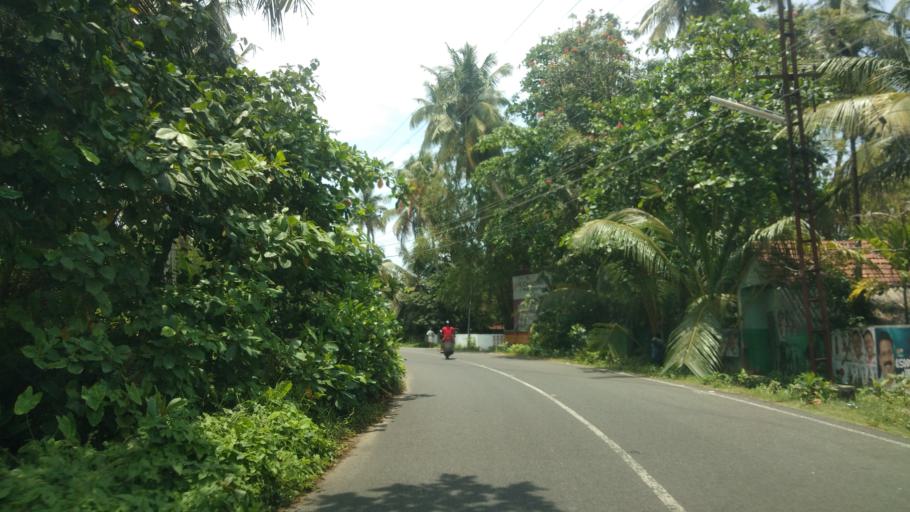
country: IN
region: Kerala
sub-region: Alappuzha
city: Arukutti
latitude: 9.8534
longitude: 76.2661
